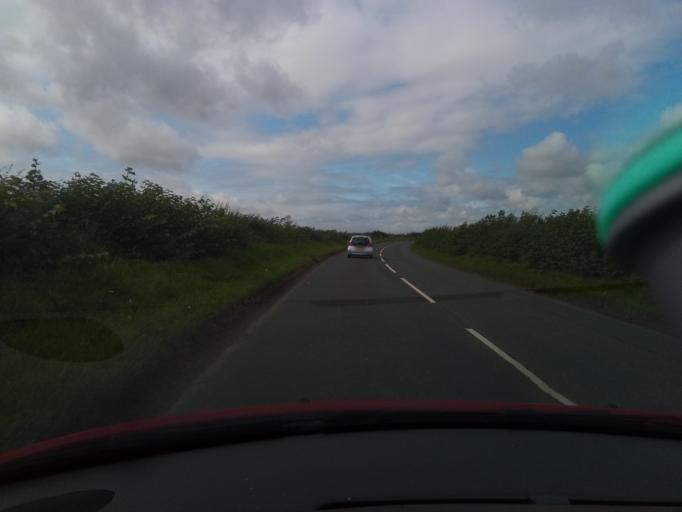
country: GB
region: Scotland
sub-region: The Scottish Borders
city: Saint Boswells
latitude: 55.5659
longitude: -2.6031
